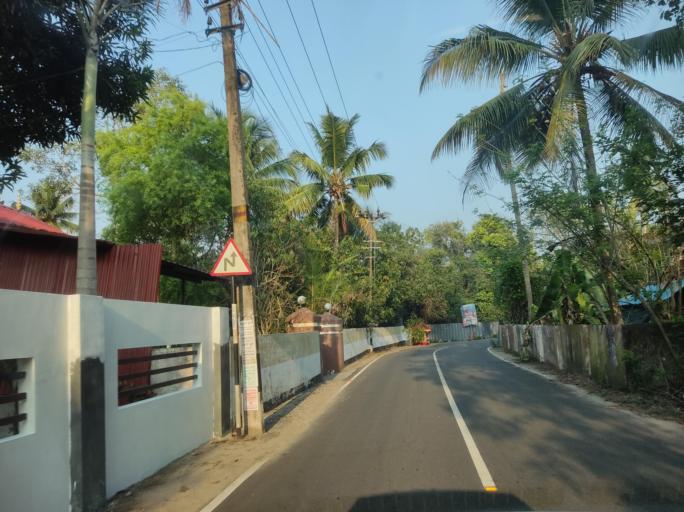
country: IN
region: Kerala
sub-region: Alappuzha
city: Alleppey
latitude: 9.5907
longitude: 76.3098
